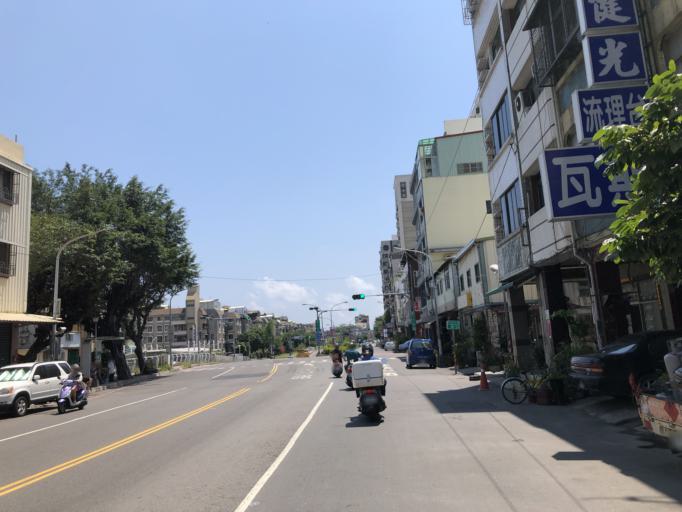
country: TW
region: Kaohsiung
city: Kaohsiung
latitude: 22.6304
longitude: 120.2809
